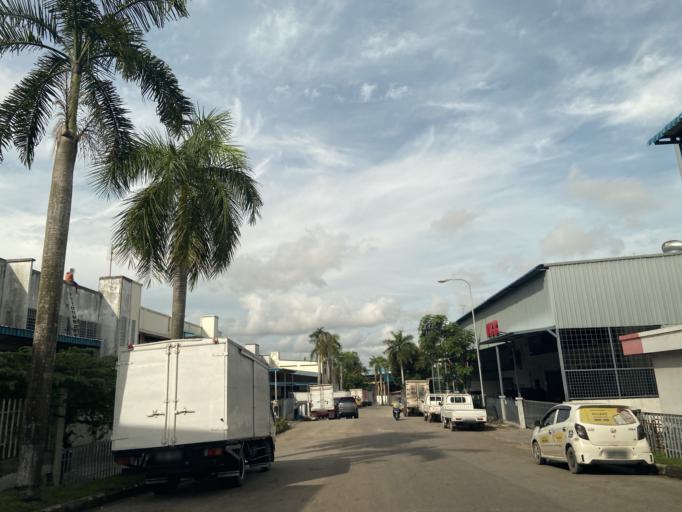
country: SG
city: Singapore
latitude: 1.1505
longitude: 104.0206
